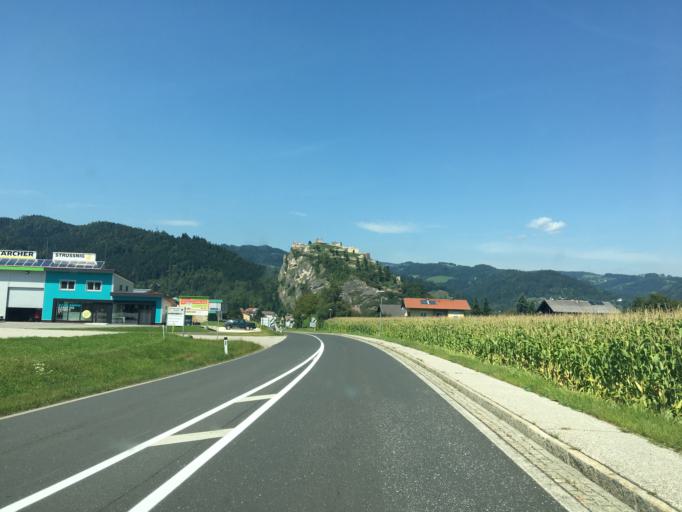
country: AT
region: Carinthia
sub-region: Politischer Bezirk Volkermarkt
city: Griffen
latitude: 46.6967
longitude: 14.7335
